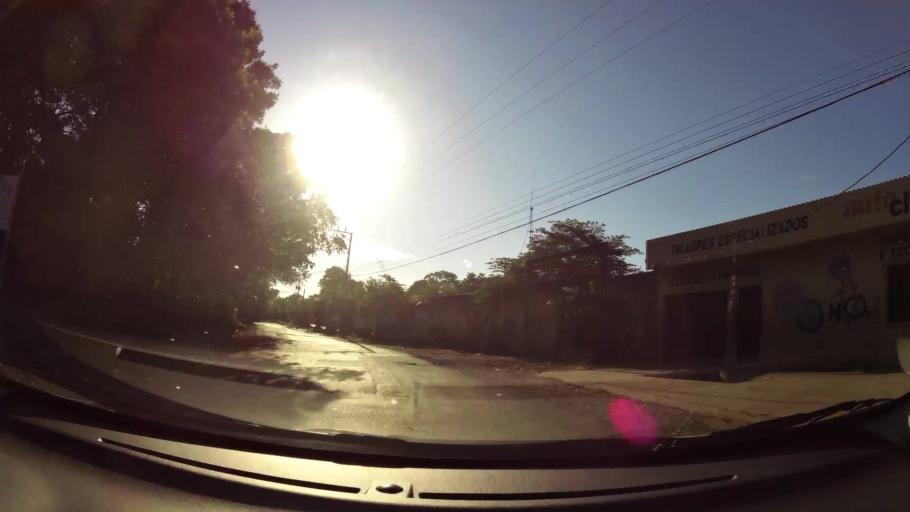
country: SV
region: Sonsonate
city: Sonsonate
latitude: 13.7085
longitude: -89.7170
